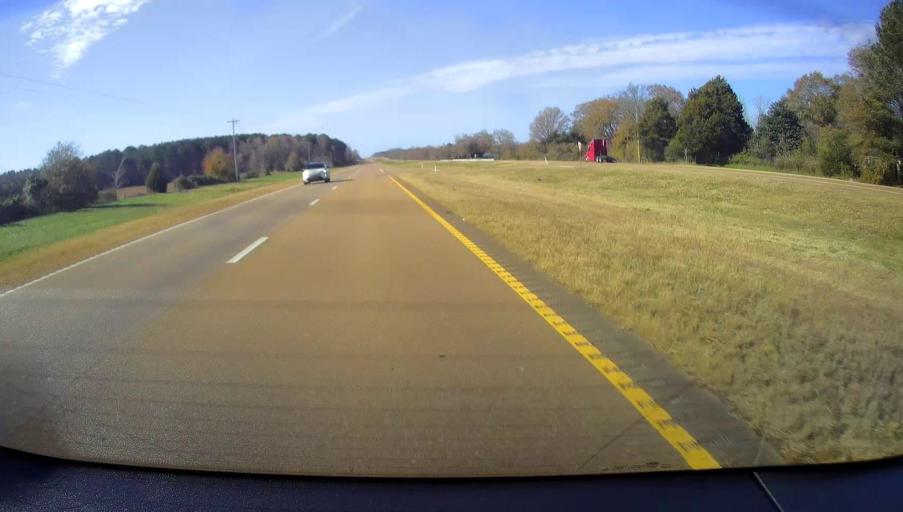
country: US
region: Mississippi
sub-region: Benton County
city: Ashland
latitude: 34.9462
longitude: -89.2178
